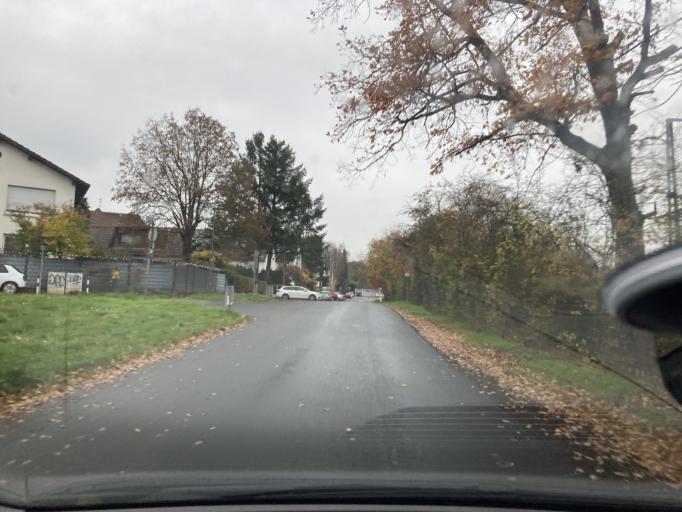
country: DE
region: Hesse
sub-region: Regierungsbezirk Darmstadt
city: Muehlheim am Main
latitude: 50.0929
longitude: 8.8063
